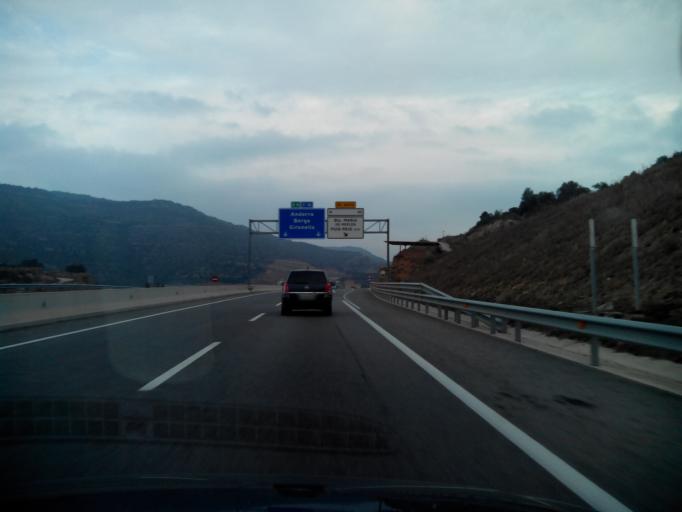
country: ES
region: Catalonia
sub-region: Provincia de Barcelona
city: Puig-reig
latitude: 41.9765
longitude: 1.8880
